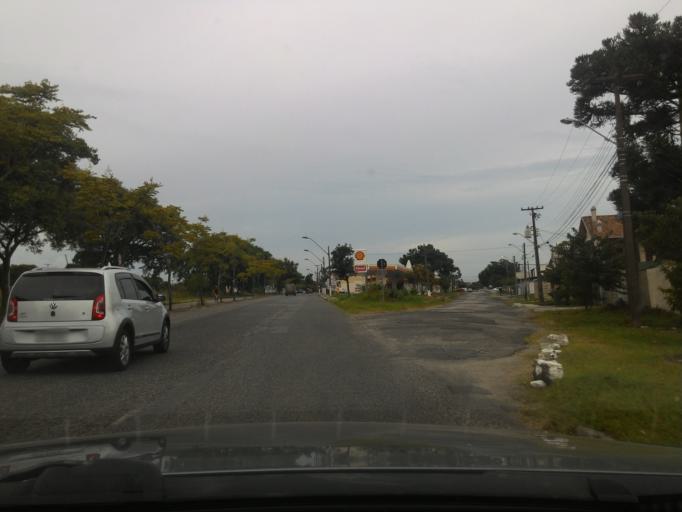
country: BR
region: Parana
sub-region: Pinhais
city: Pinhais
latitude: -25.4436
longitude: -49.2106
